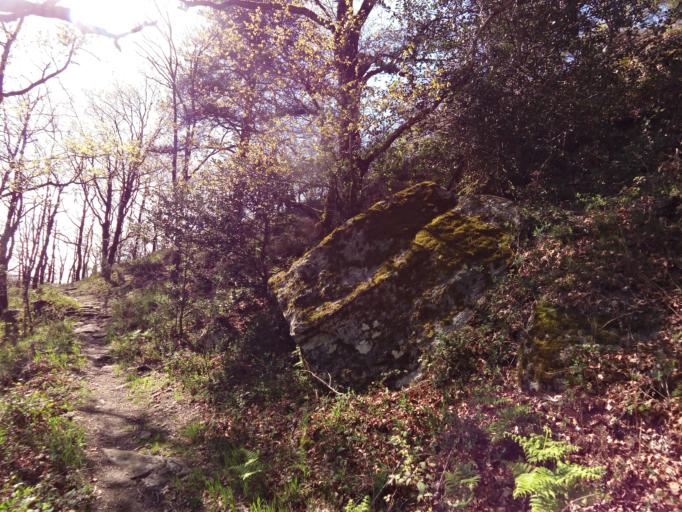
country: FR
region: Midi-Pyrenees
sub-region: Departement du Tarn
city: Soreze
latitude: 43.3751
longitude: 2.0782
